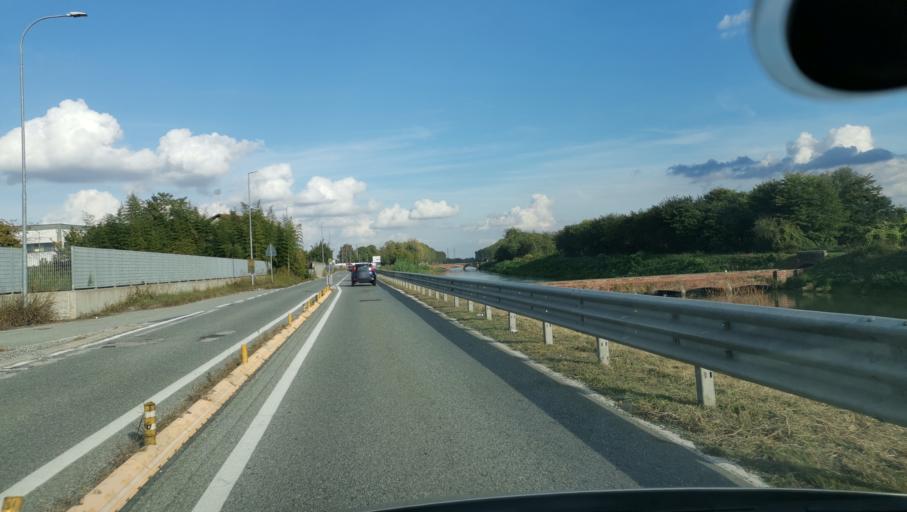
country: IT
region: Piedmont
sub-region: Provincia di Torino
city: Chivasso
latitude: 45.1924
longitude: 7.9130
